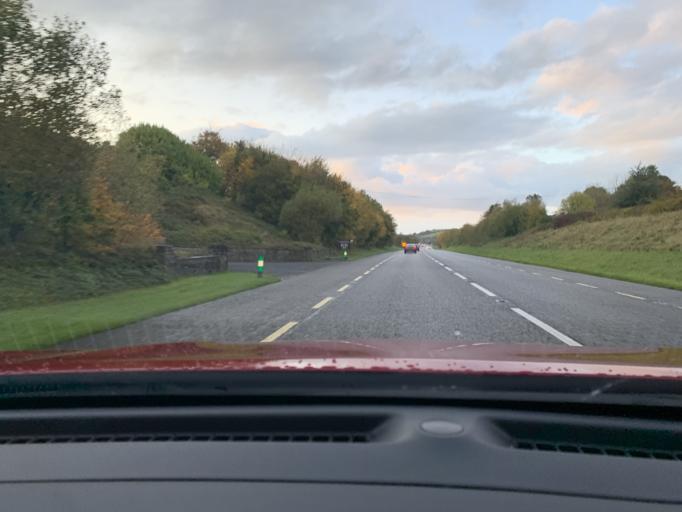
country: IE
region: Connaught
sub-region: Roscommon
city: Boyle
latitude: 54.0675
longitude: -8.3613
